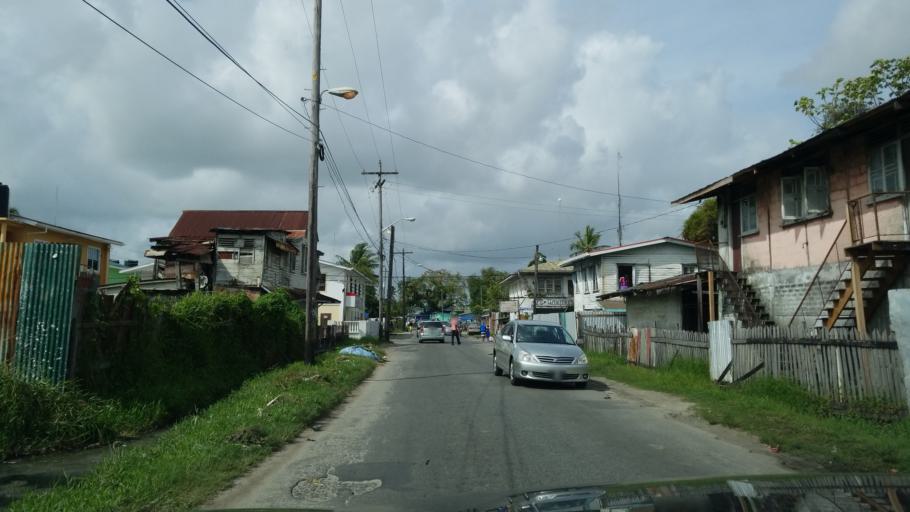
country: GY
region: Demerara-Mahaica
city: Georgetown
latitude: 6.7980
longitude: -58.1639
